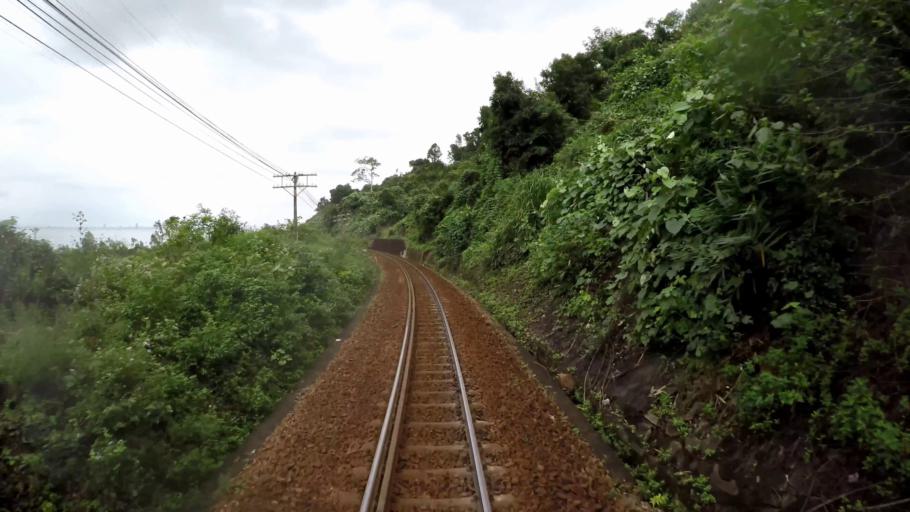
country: VN
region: Da Nang
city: Lien Chieu
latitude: 16.1595
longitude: 108.1346
